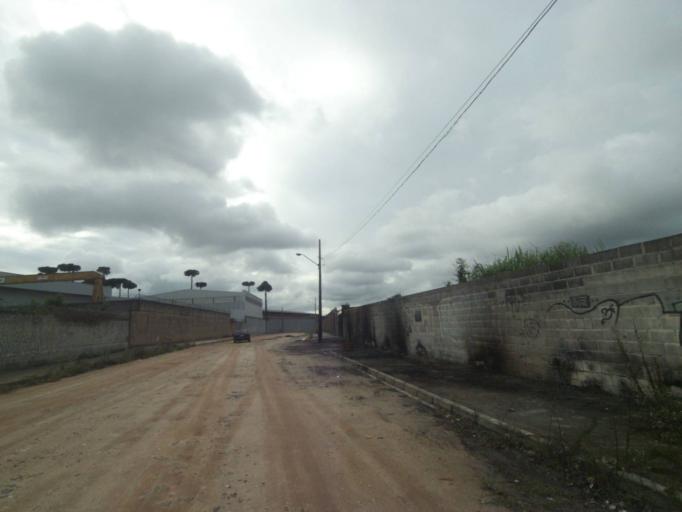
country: BR
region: Parana
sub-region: Curitiba
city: Curitiba
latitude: -25.4862
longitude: -49.3140
